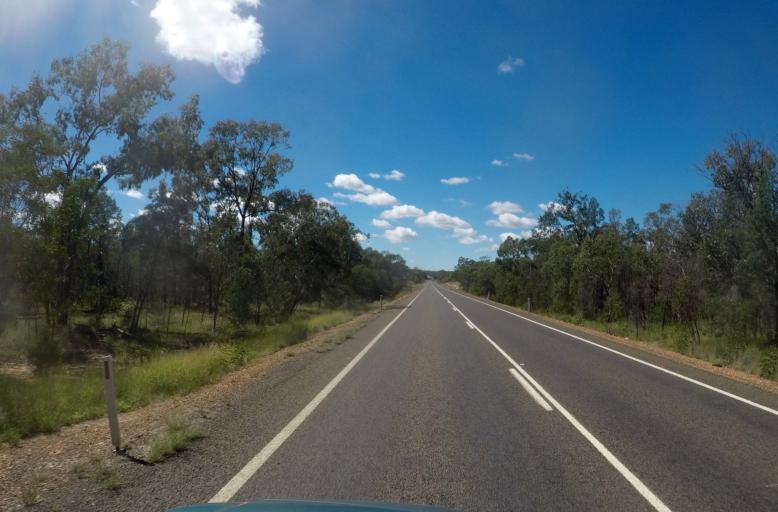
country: AU
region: Queensland
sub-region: Maranoa
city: Roma
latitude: -26.6186
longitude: 149.4286
